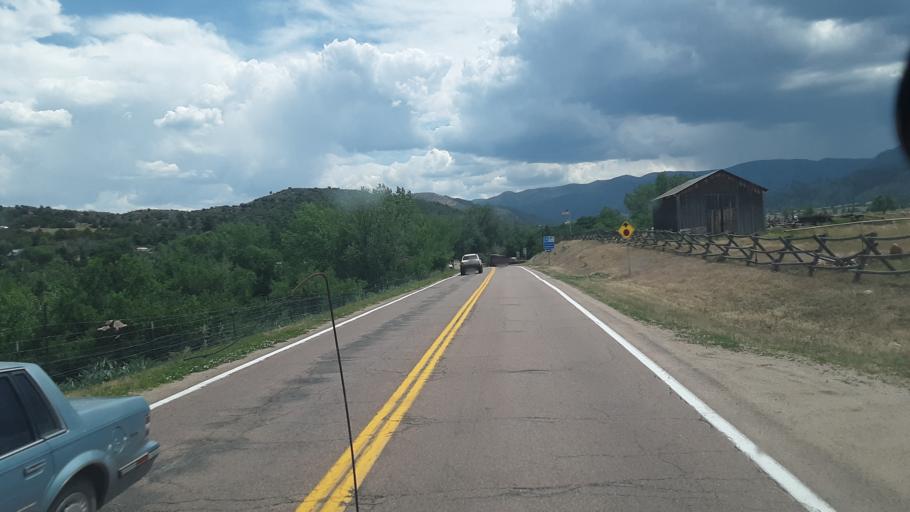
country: US
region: Colorado
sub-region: Fremont County
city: Florence
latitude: 38.2402
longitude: -105.0857
